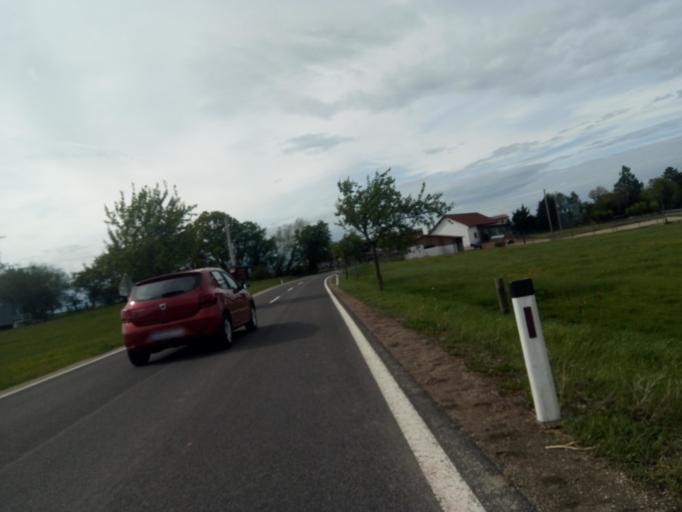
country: AT
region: Lower Austria
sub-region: Politischer Bezirk Wien-Umgebung
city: Wolfsgraben
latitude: 48.1285
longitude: 16.1147
